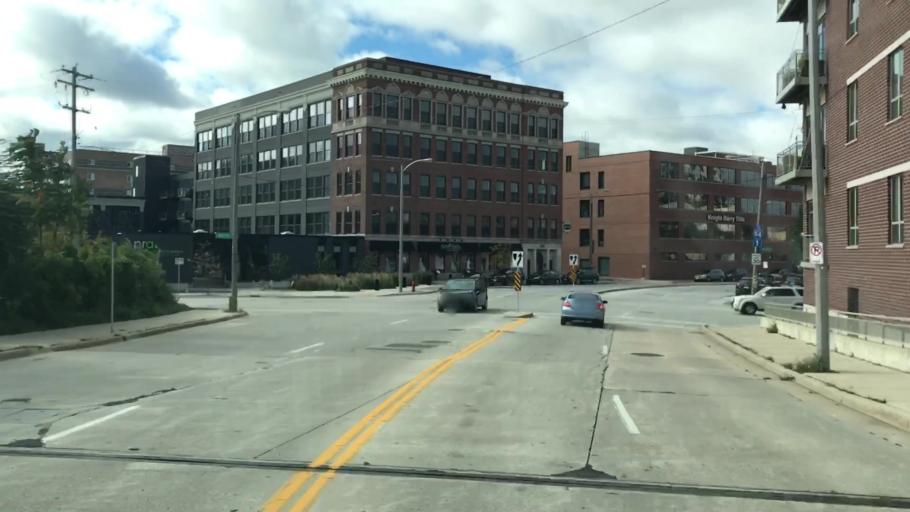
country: US
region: Wisconsin
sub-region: Milwaukee County
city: Milwaukee
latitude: 43.0298
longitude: -87.9078
